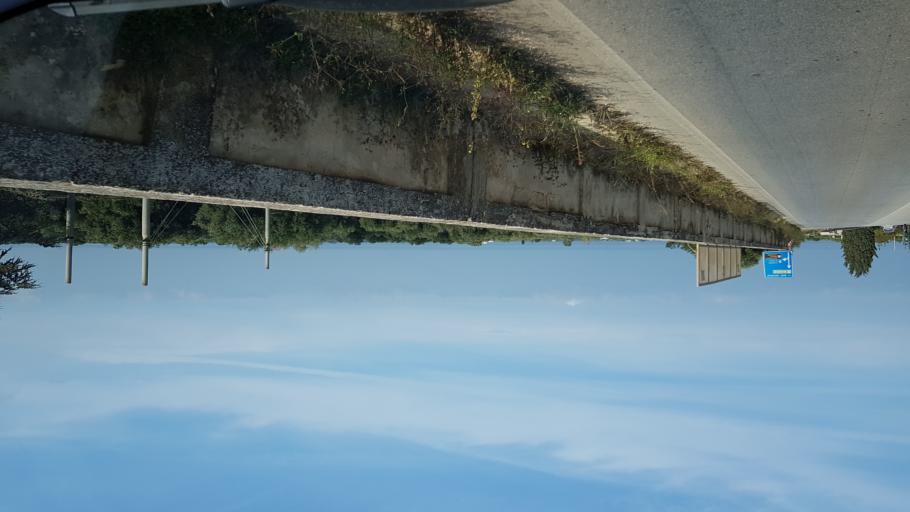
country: IT
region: Apulia
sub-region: Provincia di Brindisi
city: Ostuni
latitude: 40.7515
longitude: 17.5826
